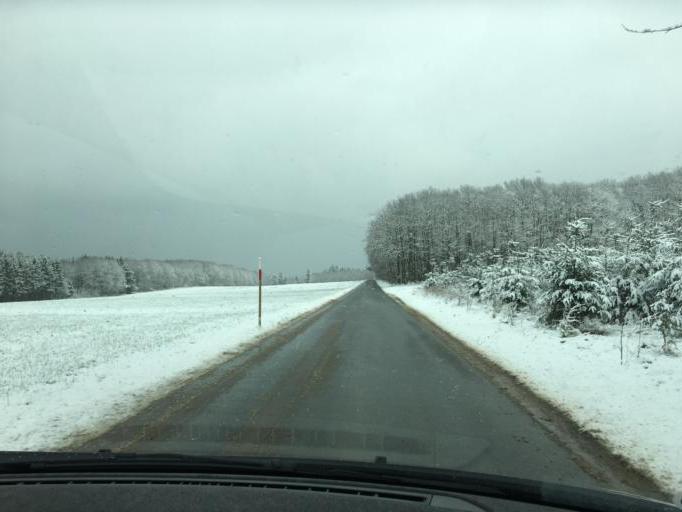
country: DE
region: North Rhine-Westphalia
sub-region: Regierungsbezirk Koln
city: Hurtgenwald
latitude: 50.7325
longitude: 6.4147
